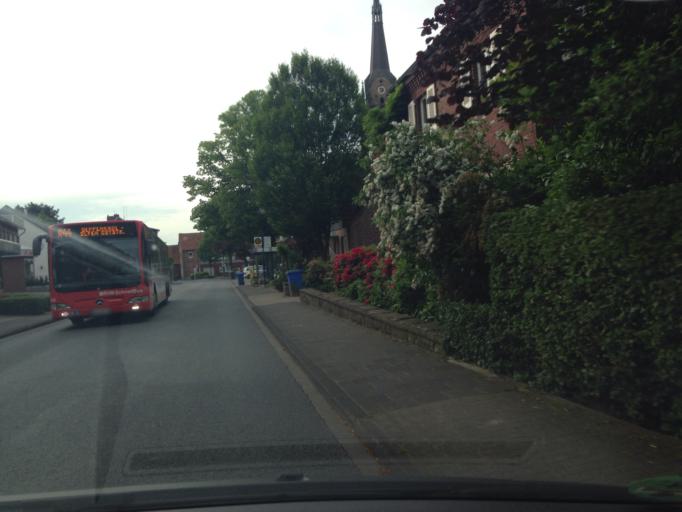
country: DE
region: North Rhine-Westphalia
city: Ludinghausen
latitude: 51.7610
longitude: 7.3958
